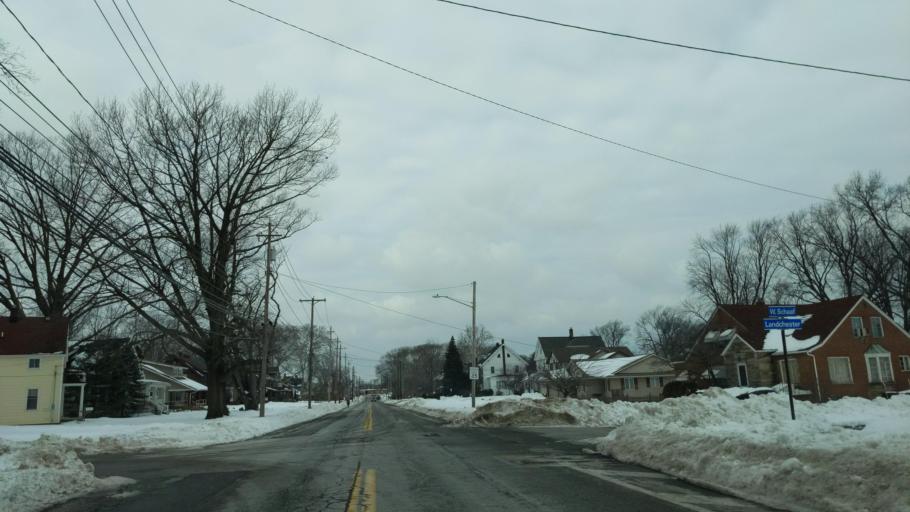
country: US
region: Ohio
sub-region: Cuyahoga County
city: Brooklyn Heights
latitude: 41.4274
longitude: -81.6922
